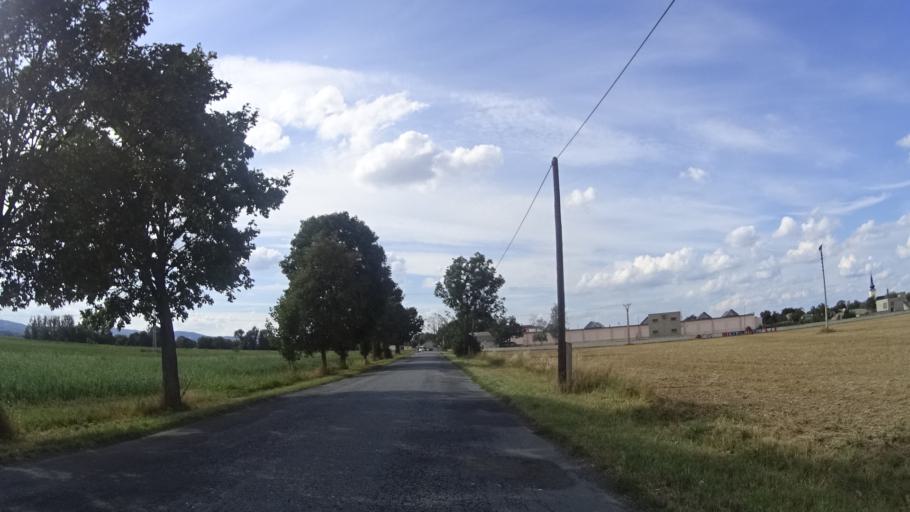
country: CZ
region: Olomoucky
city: Moravicany
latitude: 49.7513
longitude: 16.9685
